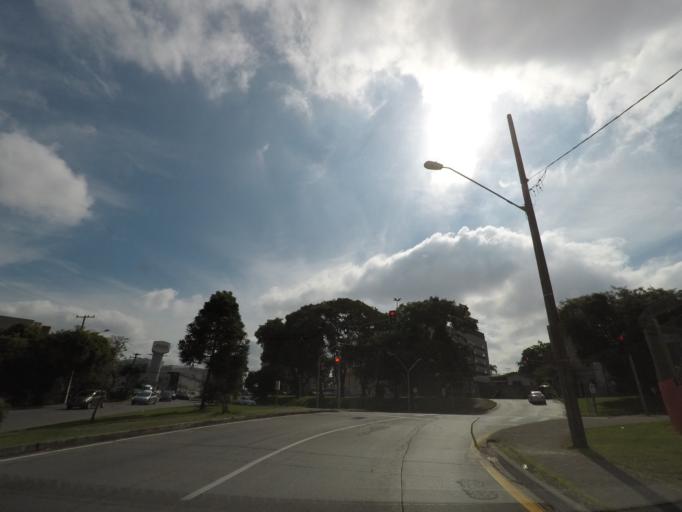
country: BR
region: Parana
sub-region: Curitiba
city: Curitiba
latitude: -25.4781
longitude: -49.2854
